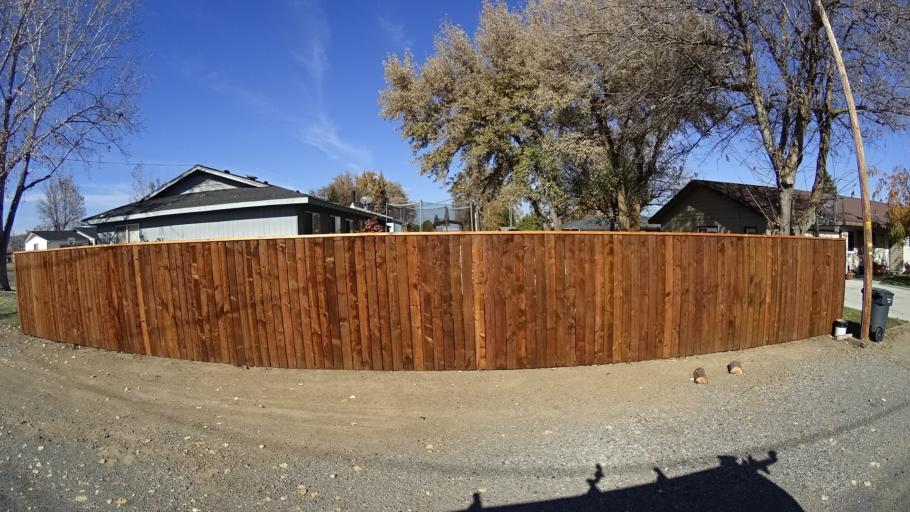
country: US
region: California
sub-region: Siskiyou County
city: Montague
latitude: 41.6433
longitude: -122.5247
